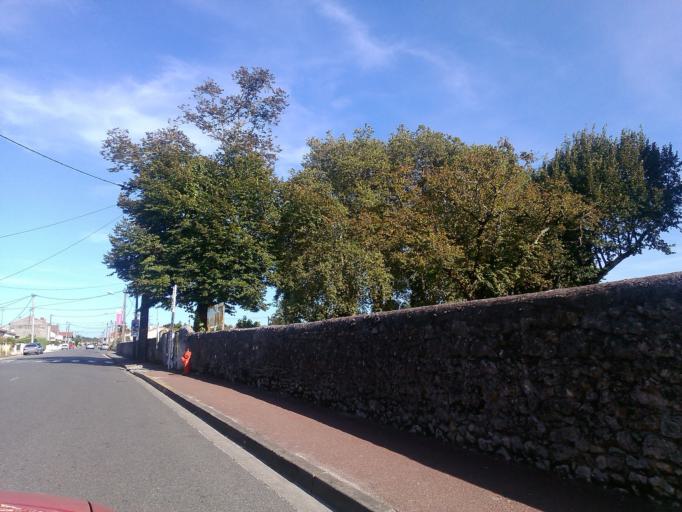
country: FR
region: Aquitaine
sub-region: Departement de la Gironde
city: Hourtin
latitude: 45.1858
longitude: -1.0560
